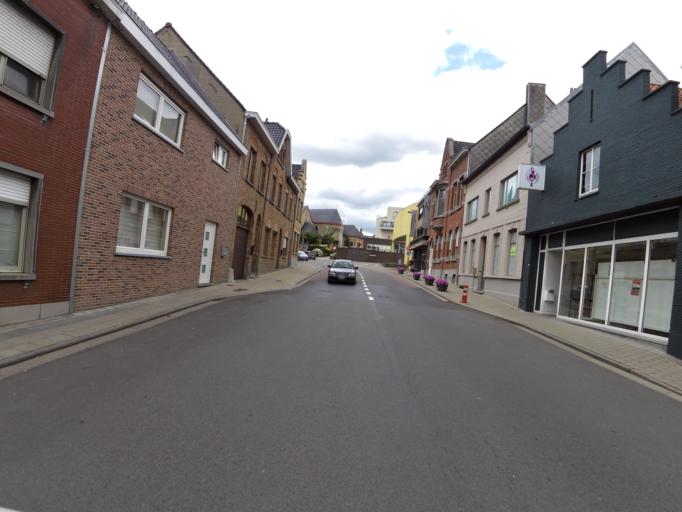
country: BE
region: Flanders
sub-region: Provincie West-Vlaanderen
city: Hooglede
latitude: 50.9773
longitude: 3.0832
